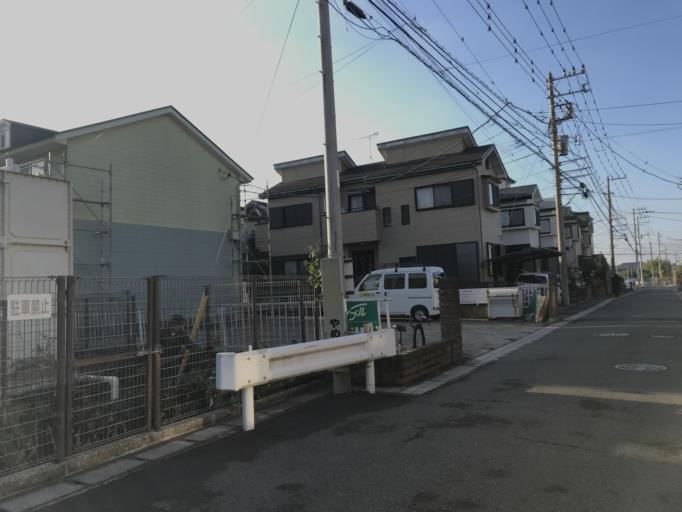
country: JP
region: Chiba
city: Funabashi
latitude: 35.7274
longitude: 139.9691
